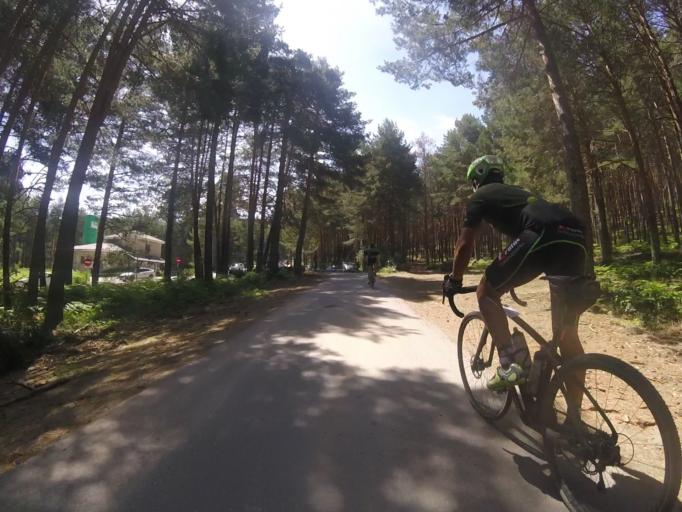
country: ES
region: Castille and Leon
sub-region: Provincia de Segovia
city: San Ildefonso
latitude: 40.8212
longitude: -4.0174
